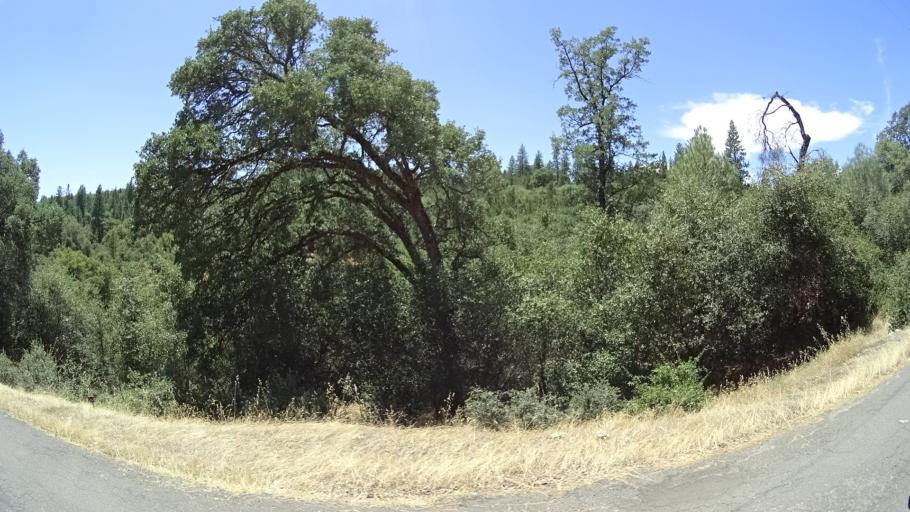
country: US
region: California
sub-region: Calaveras County
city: Forest Meadows
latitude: 38.2090
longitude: -120.4605
